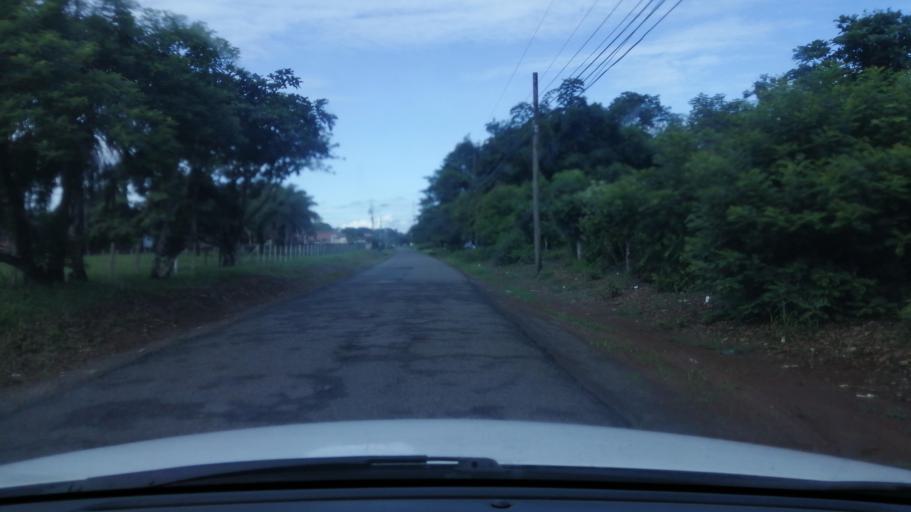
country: PA
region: Chiriqui
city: El Quiteno
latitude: 8.4640
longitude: -82.4158
